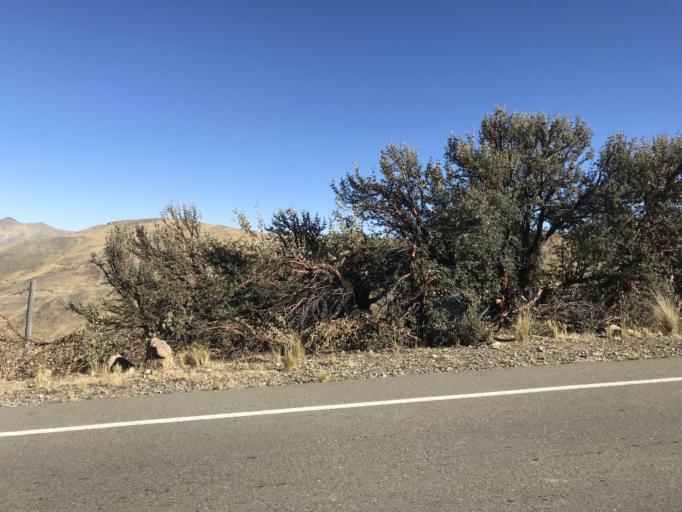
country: PE
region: Puno
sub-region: Yunguyo
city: Yunguyo
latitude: -16.1742
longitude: -68.9828
